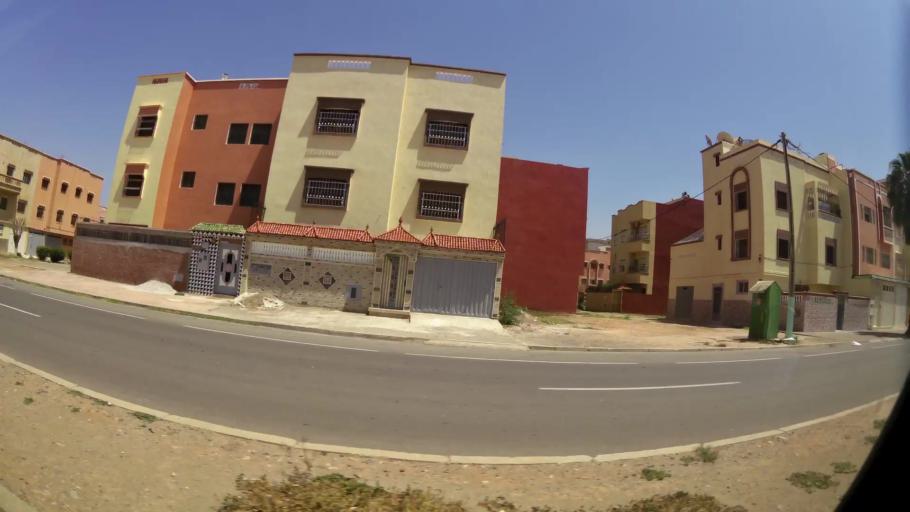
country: MA
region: Souss-Massa-Draa
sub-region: Inezgane-Ait Mellou
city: Inezgane
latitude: 30.3483
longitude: -9.4855
